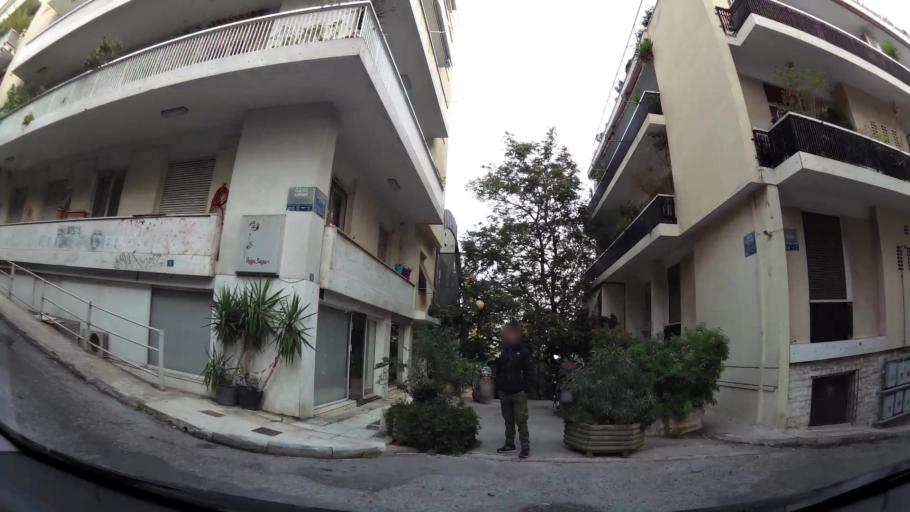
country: GR
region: Attica
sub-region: Nomarchia Athinas
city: Kipseli
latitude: 37.9817
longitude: 23.7397
